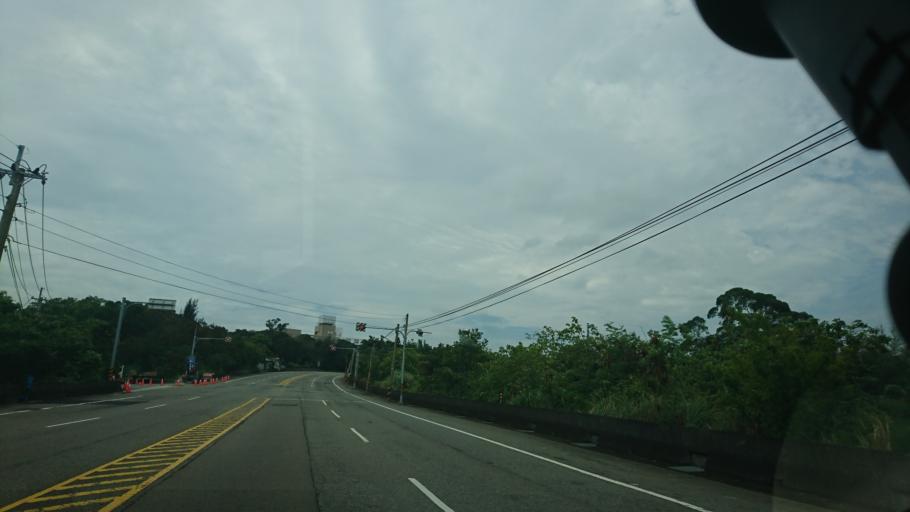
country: TW
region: Taiwan
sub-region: Miaoli
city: Miaoli
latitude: 24.5162
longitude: 120.7876
